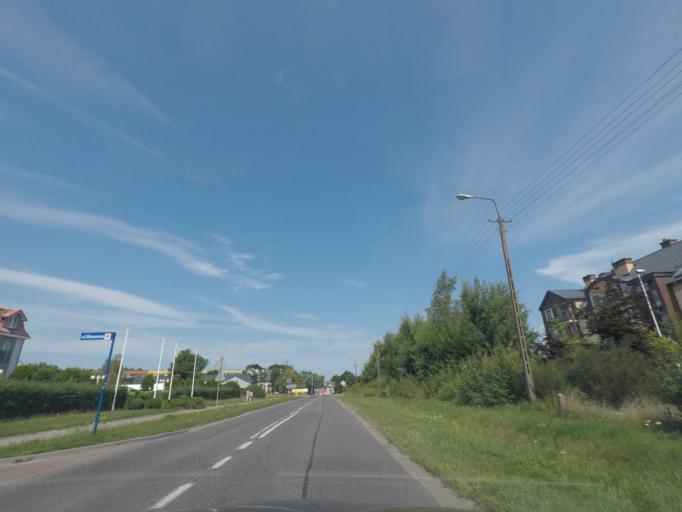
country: PL
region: Pomeranian Voivodeship
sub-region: Powiat slupski
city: Ustka
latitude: 54.5741
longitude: 16.8524
